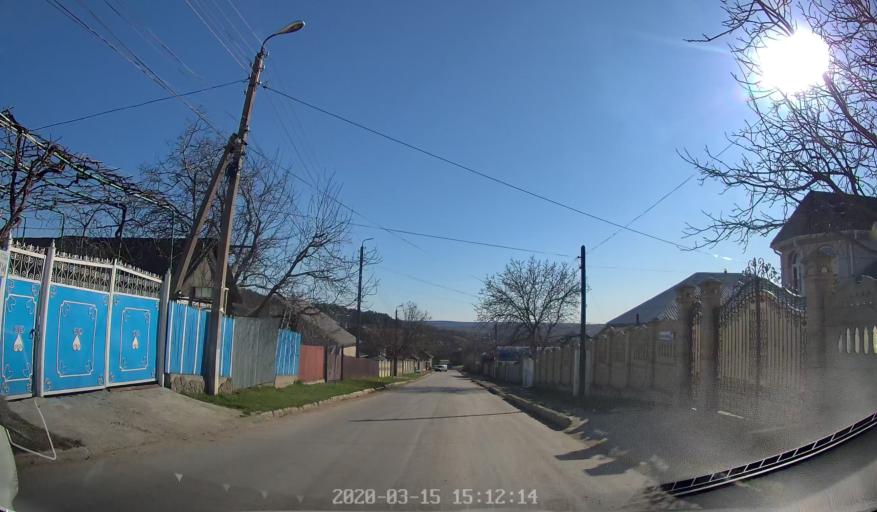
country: MD
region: Orhei
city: Orhei
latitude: 47.2568
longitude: 28.7741
